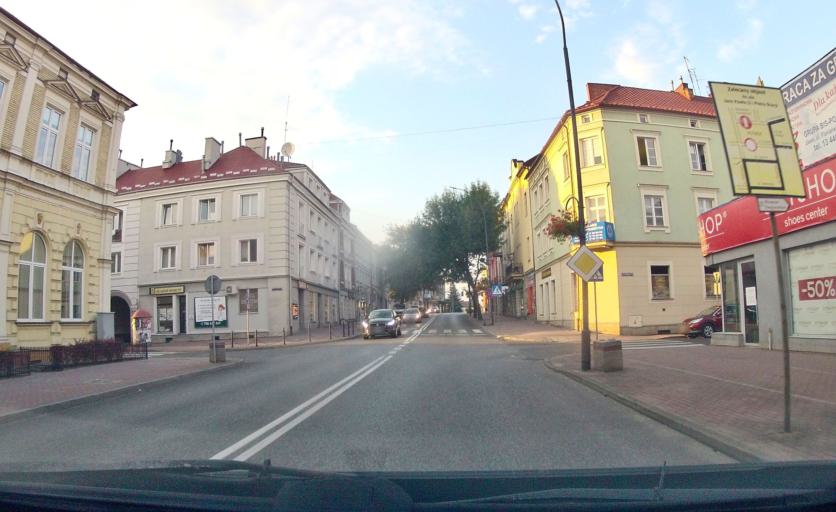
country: PL
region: Subcarpathian Voivodeship
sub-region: Powiat jasielski
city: Jaslo
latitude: 49.7454
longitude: 21.4735
